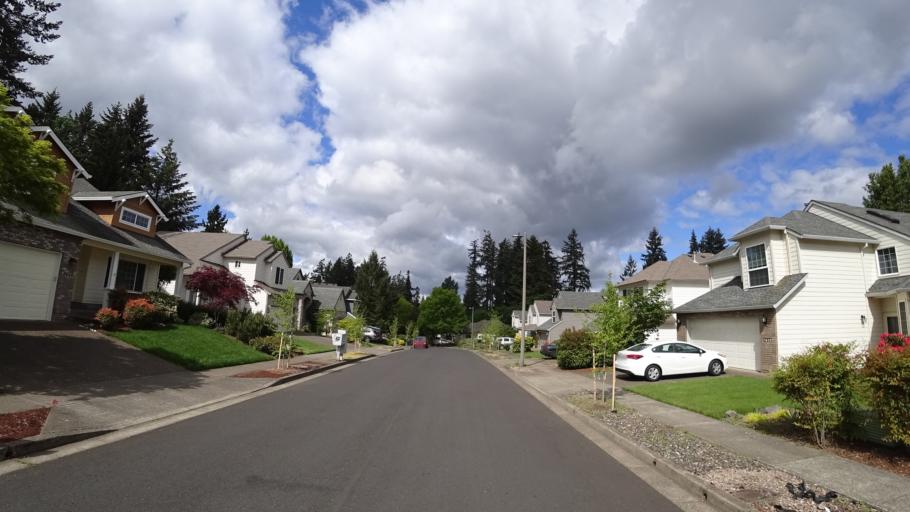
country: US
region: Oregon
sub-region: Washington County
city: Beaverton
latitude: 45.4645
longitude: -122.8326
